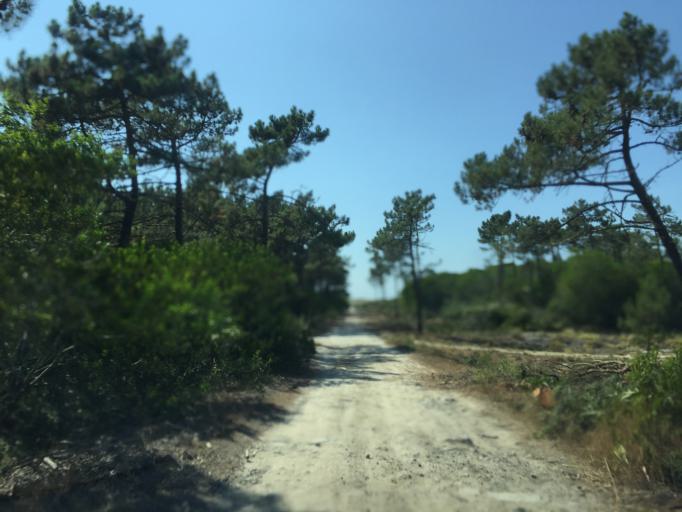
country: PT
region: Coimbra
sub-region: Figueira da Foz
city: Tavarede
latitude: 40.2632
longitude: -8.8625
